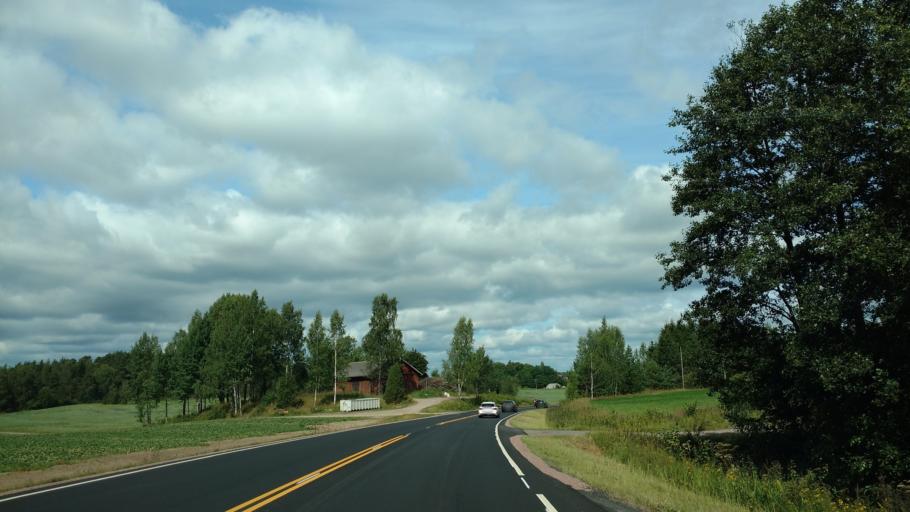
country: FI
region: Varsinais-Suomi
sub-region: Salo
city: Saerkisalo
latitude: 60.1784
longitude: 22.9023
